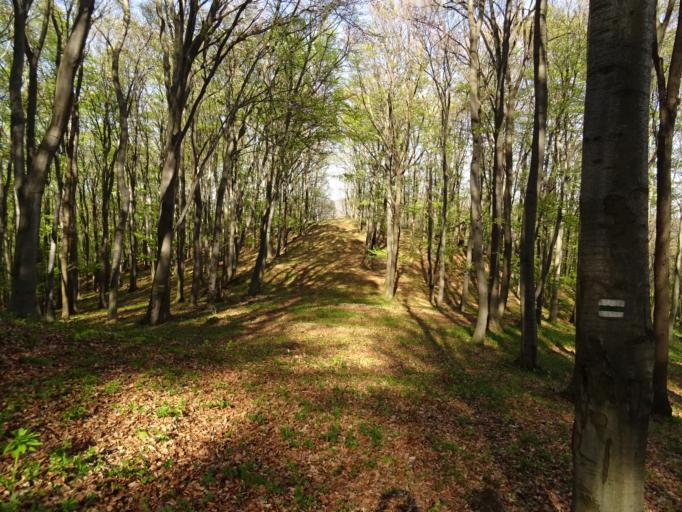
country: HU
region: Borsod-Abauj-Zemplen
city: Gonc
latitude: 48.5602
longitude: 21.3838
